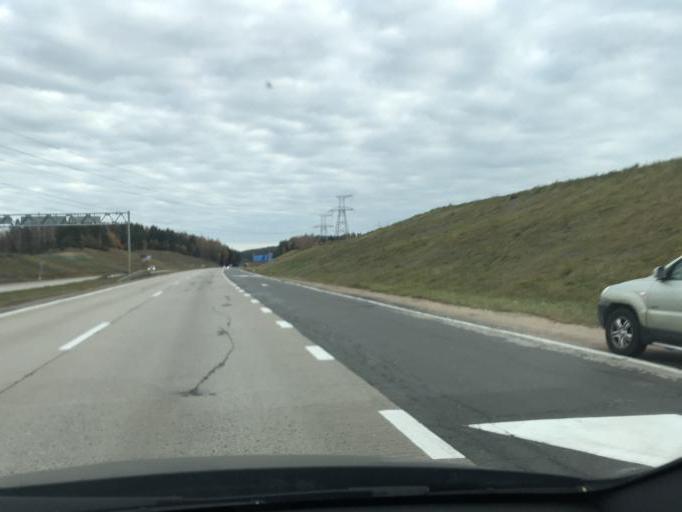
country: BY
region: Minsk
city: Astrashytski Haradok
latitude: 54.0576
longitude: 27.7065
